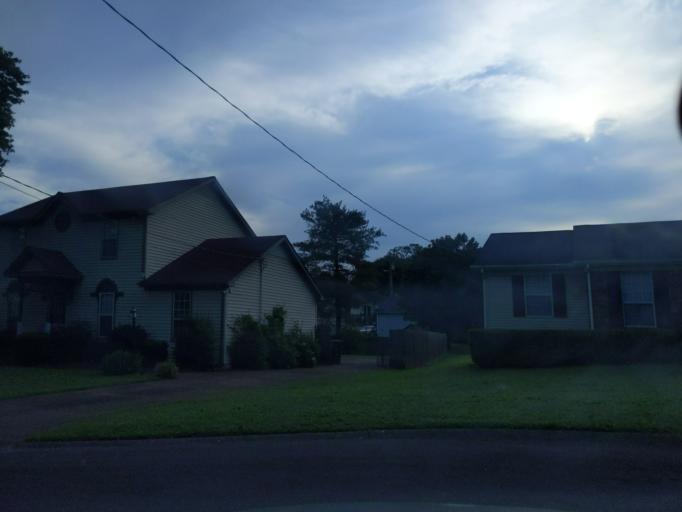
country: US
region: Tennessee
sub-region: Davidson County
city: Lakewood
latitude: 36.1866
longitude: -86.6047
